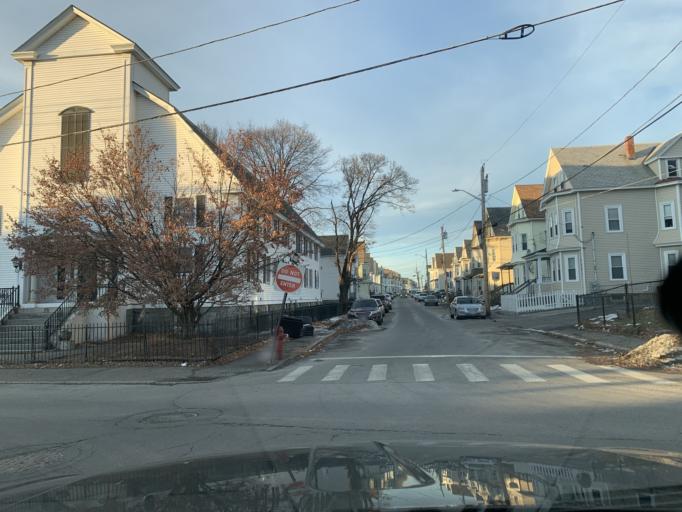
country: US
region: Massachusetts
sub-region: Middlesex County
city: Lowell
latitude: 42.6363
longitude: -71.2994
